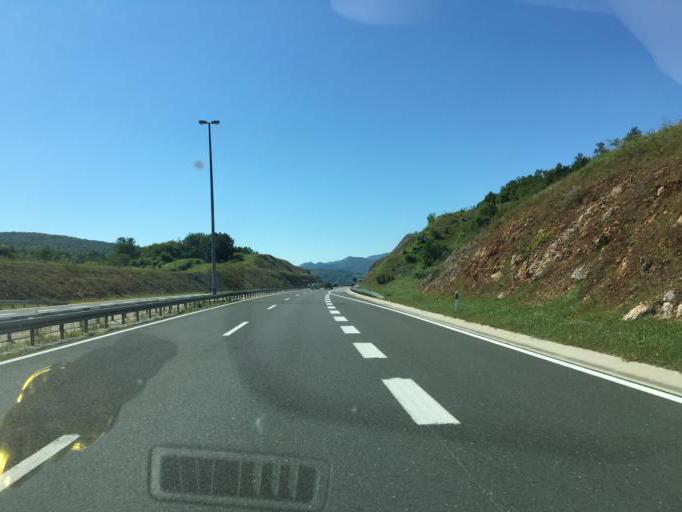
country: HR
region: Licko-Senjska
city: Otocac
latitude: 44.9186
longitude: 15.1689
